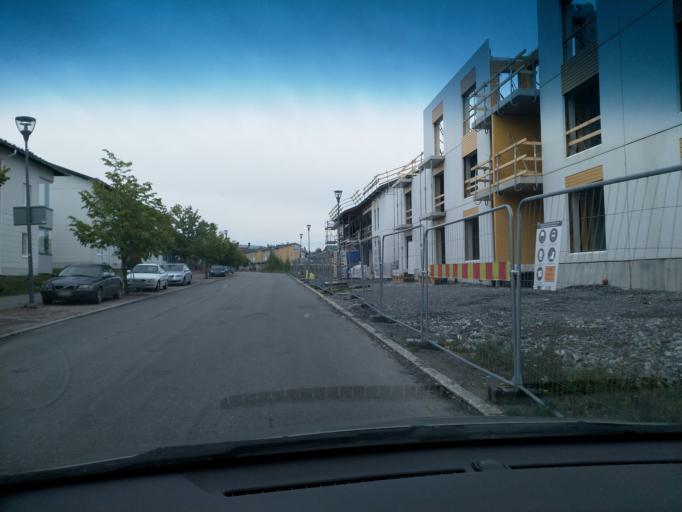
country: FI
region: Pirkanmaa
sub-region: Tampere
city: Tampere
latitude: 61.4769
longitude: 23.8273
